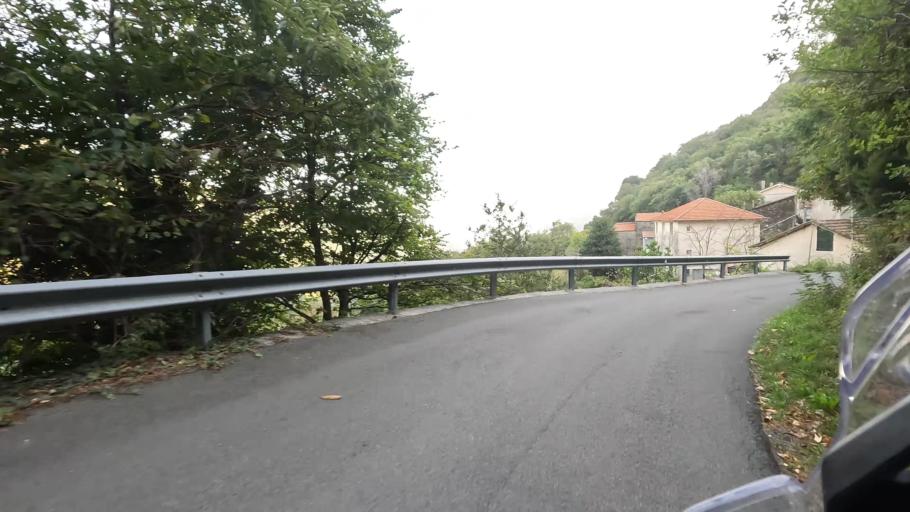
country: IT
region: Liguria
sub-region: Provincia di Savona
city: San Giovanni
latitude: 44.4006
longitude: 8.5326
